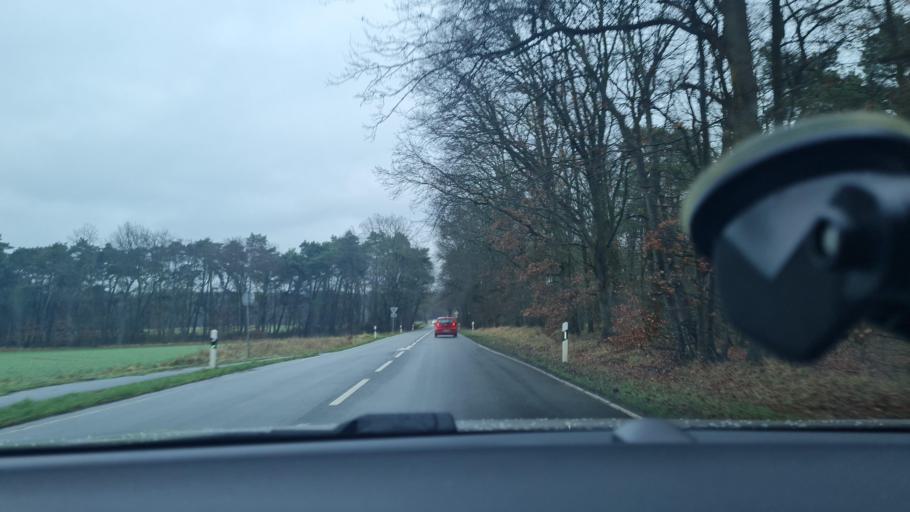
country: DE
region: North Rhine-Westphalia
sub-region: Regierungsbezirk Dusseldorf
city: Hunxe
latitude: 51.6776
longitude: 6.7399
